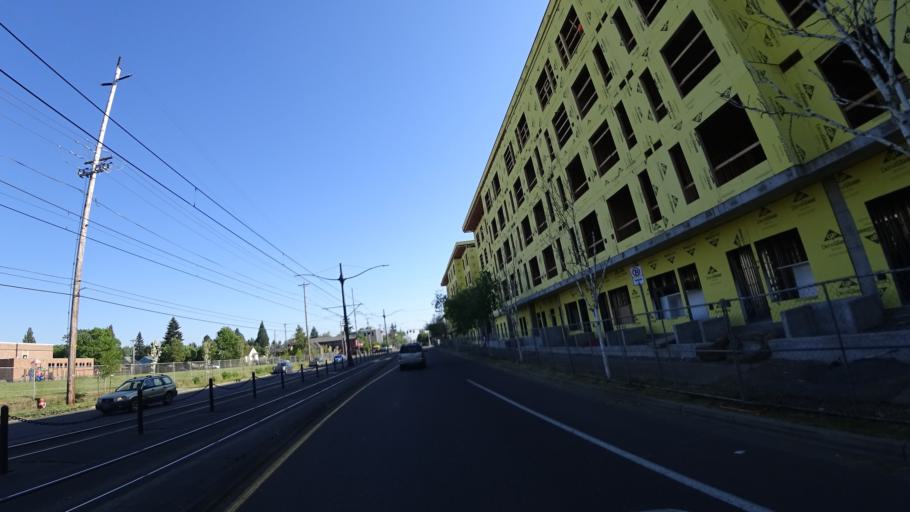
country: US
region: Oregon
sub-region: Multnomah County
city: Portland
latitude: 45.5675
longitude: -122.6823
